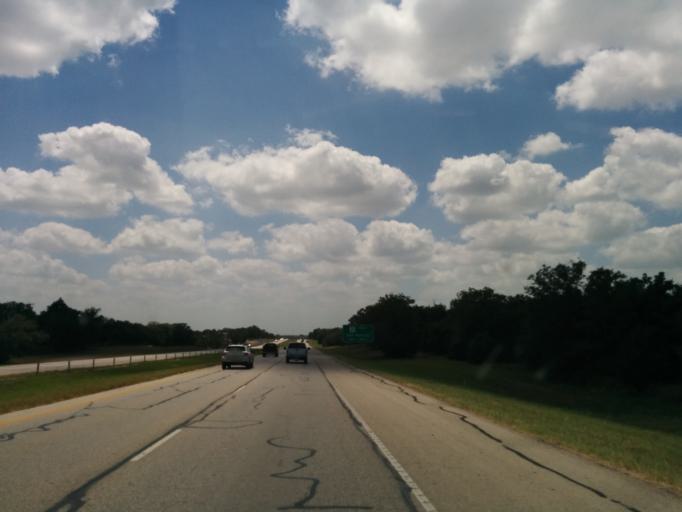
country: US
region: Texas
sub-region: Bastrop County
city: Bastrop
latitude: 30.1109
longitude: -97.3931
